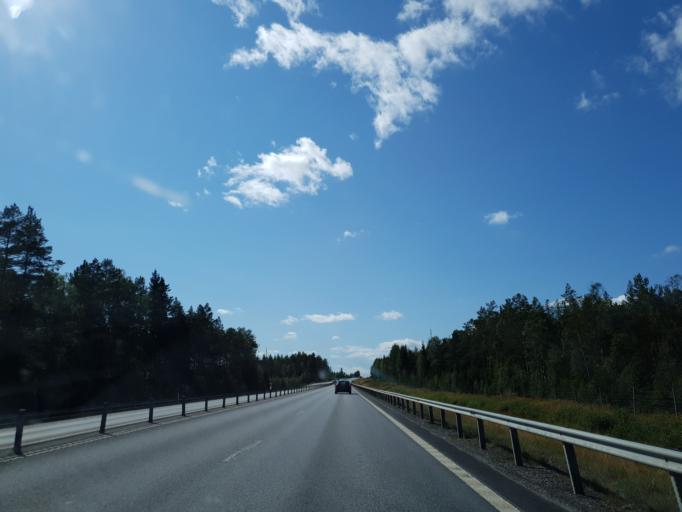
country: SE
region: Vaesterbotten
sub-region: Umea Kommun
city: Hoernefors
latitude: 63.6587
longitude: 19.9587
